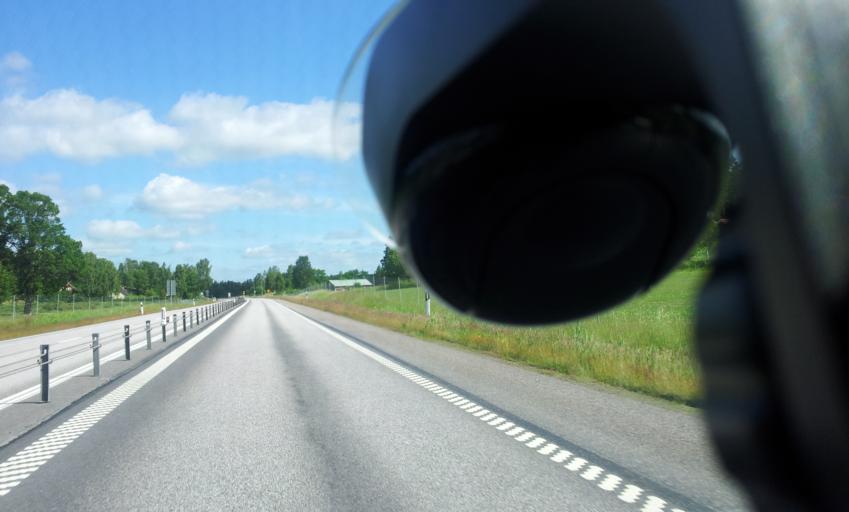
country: SE
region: OEstergoetland
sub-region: Soderkopings Kommun
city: Soederkoeping
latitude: 58.4066
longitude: 16.4013
